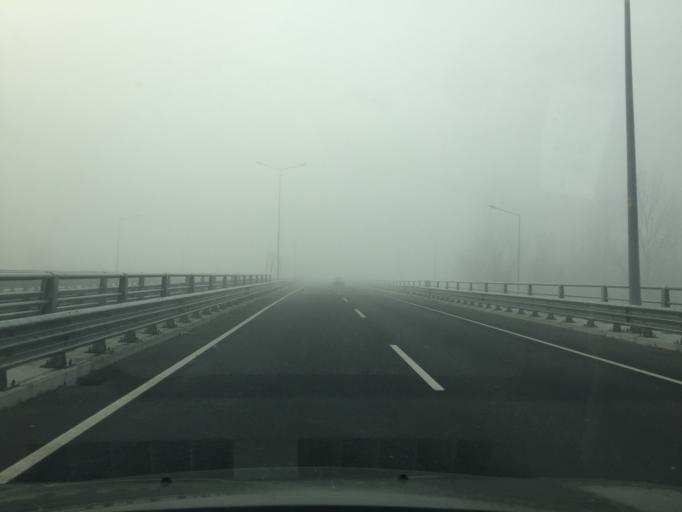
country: TR
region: Duzce
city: Duzce
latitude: 40.8259
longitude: 31.1666
